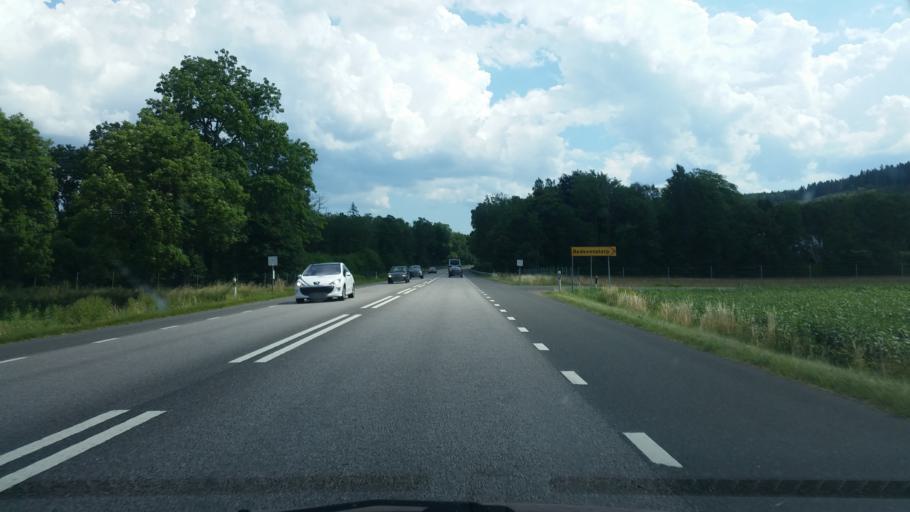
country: SE
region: Vaestra Goetaland
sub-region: Skara Kommun
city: Axvall
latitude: 58.3830
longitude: 13.6727
